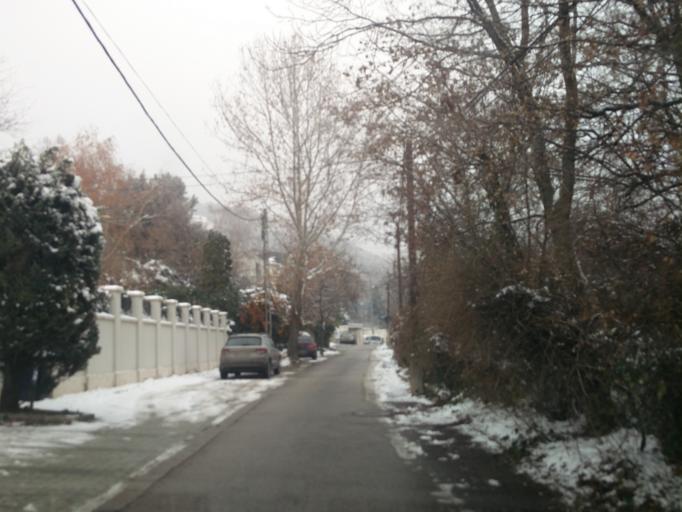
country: HU
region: Budapest
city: Budapest III. keruelet
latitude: 47.5387
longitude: 19.0208
